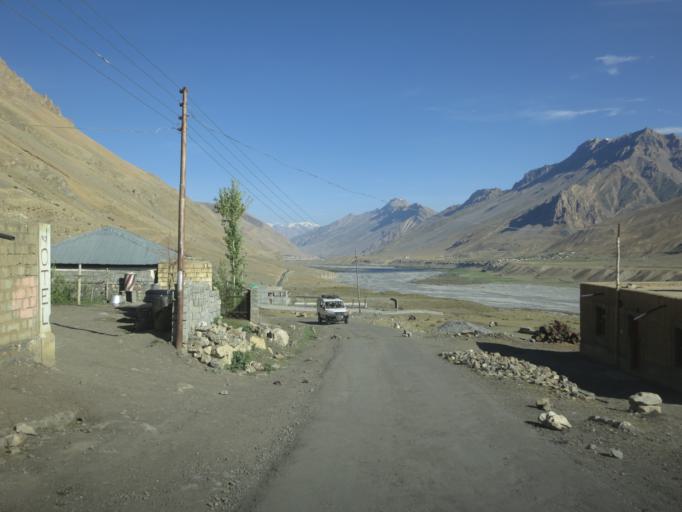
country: IN
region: Himachal Pradesh
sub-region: Shimla
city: Sarahan
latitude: 32.2891
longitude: 78.0133
